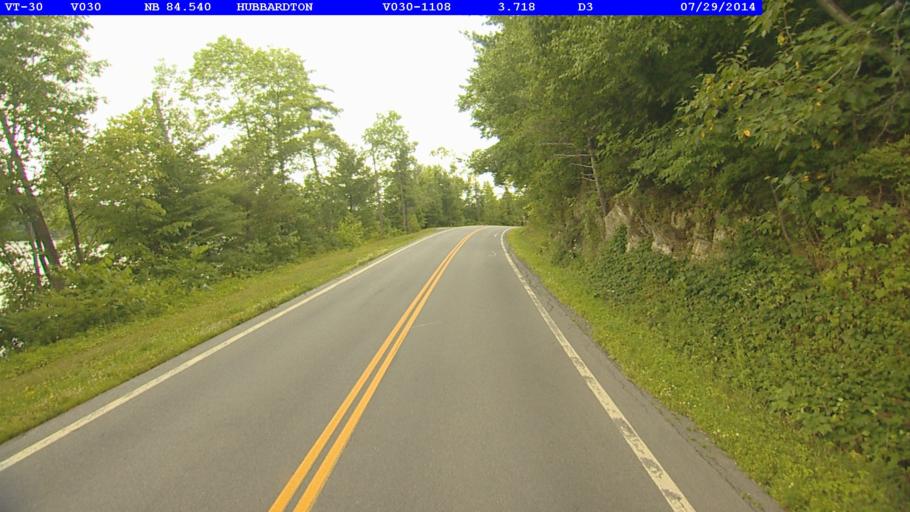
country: US
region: Vermont
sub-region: Rutland County
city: Brandon
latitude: 43.7311
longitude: -73.1805
